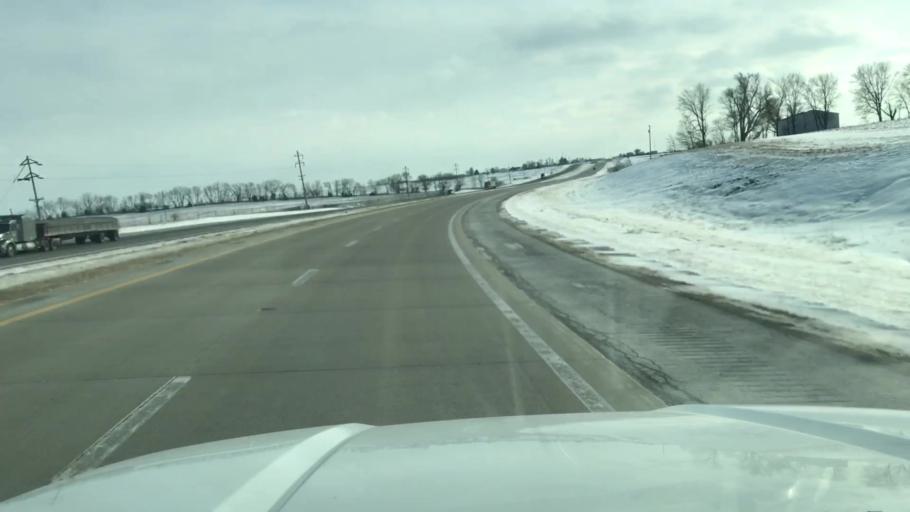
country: US
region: Missouri
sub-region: Nodaway County
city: Maryville
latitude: 40.2711
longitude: -94.8670
